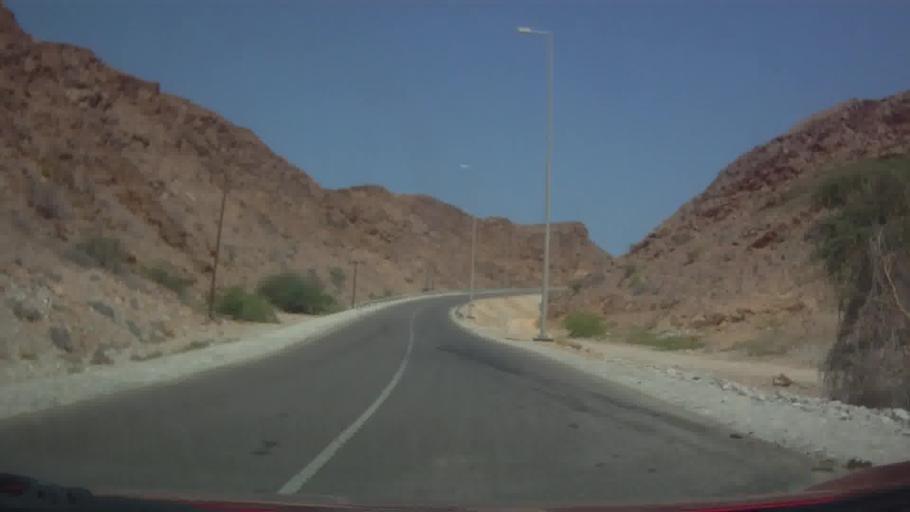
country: OM
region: Muhafazat Masqat
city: Muscat
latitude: 23.5127
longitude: 58.6786
